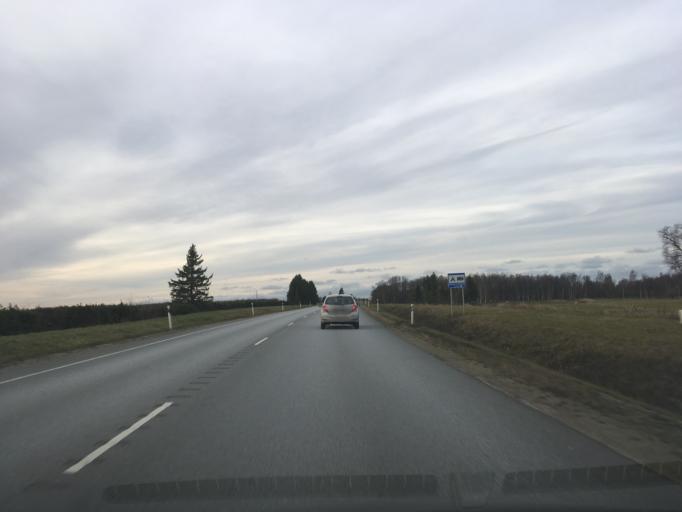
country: EE
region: Ida-Virumaa
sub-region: Kivioli linn
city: Kivioli
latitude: 59.4154
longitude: 26.9798
